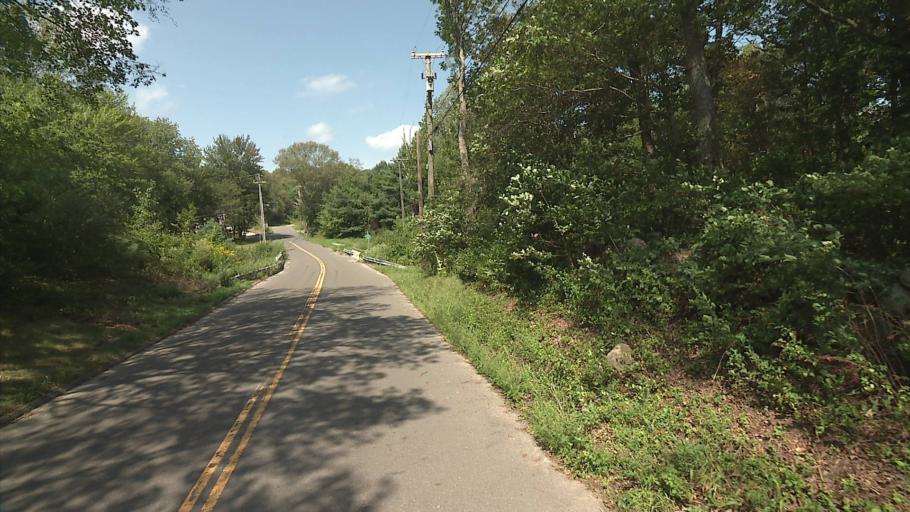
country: US
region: Connecticut
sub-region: New London County
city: Niantic
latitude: 41.3568
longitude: -72.2605
